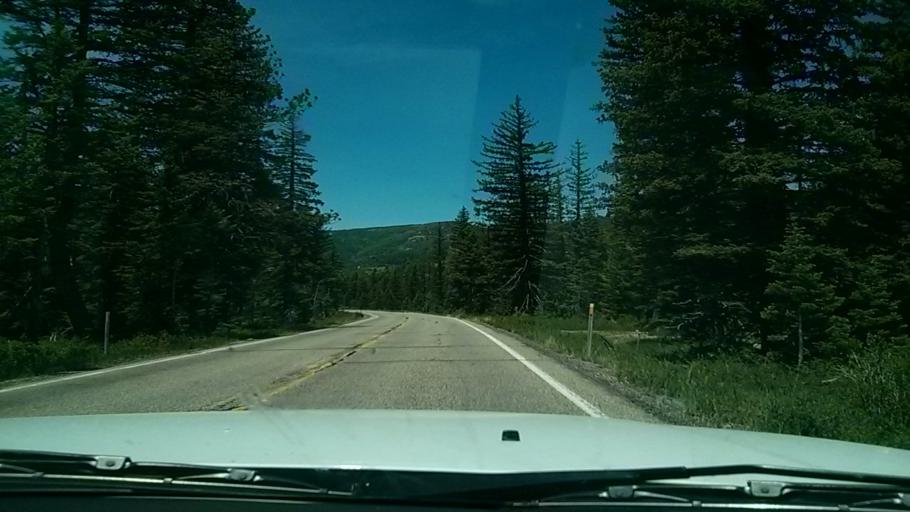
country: US
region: Utah
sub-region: Iron County
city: Cedar City
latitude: 37.5938
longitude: -112.9105
